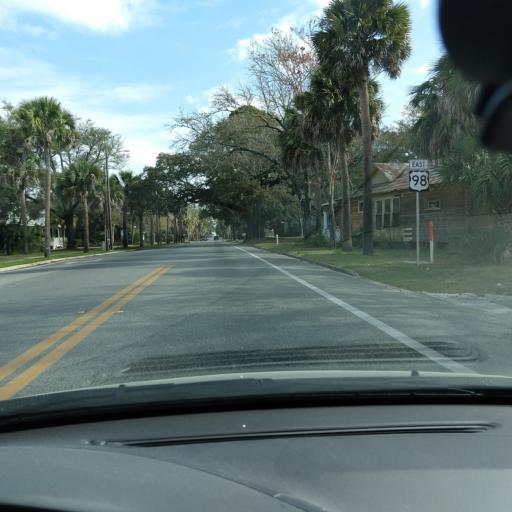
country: US
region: Florida
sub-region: Franklin County
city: Apalachicola
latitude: 29.7163
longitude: -84.9975
